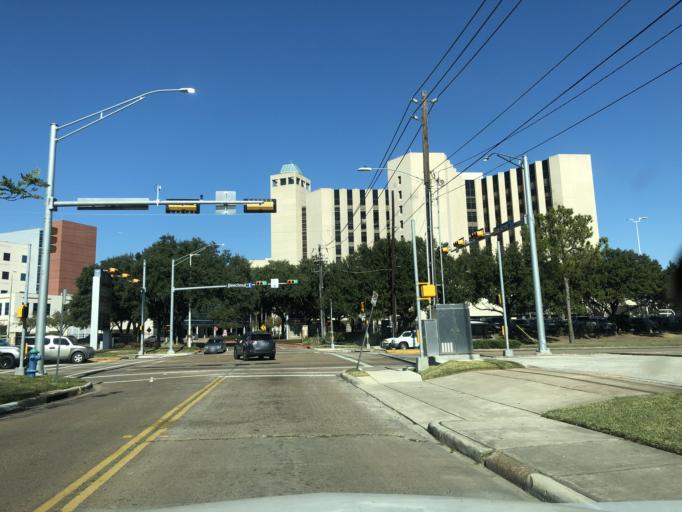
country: US
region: Texas
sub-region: Harris County
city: Bellaire
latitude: 29.6913
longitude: -95.5219
